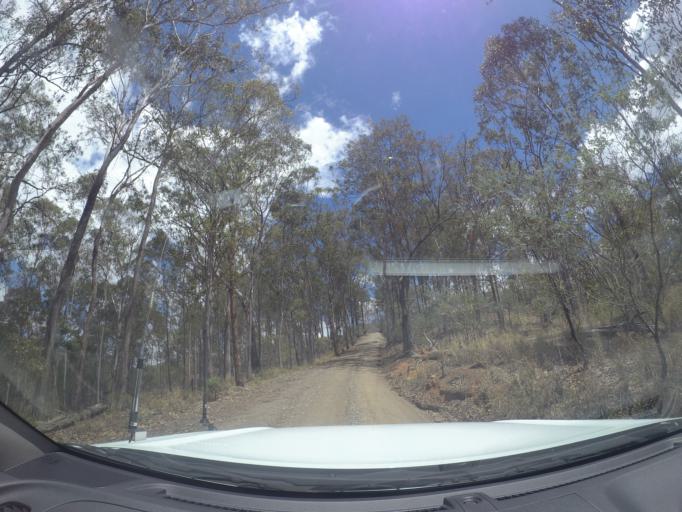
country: AU
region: Queensland
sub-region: Logan
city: Cedar Vale
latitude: -27.9160
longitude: 153.0491
